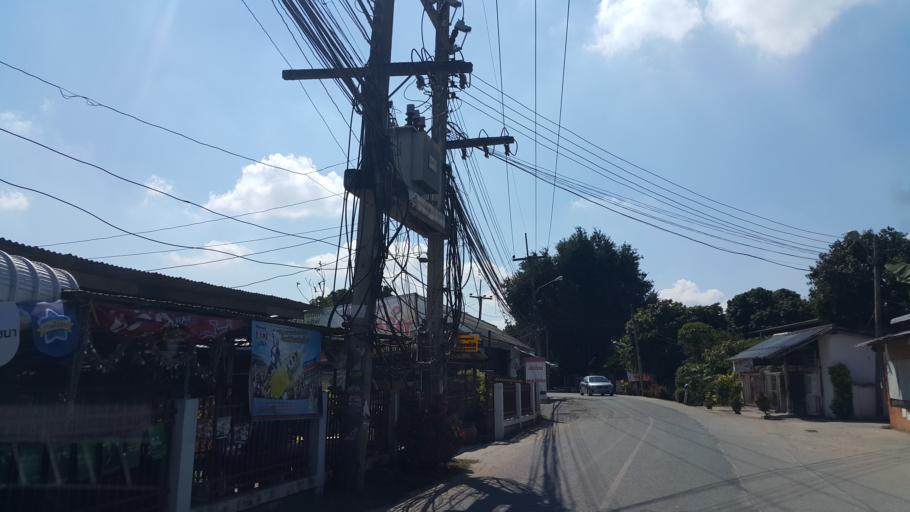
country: TH
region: Chiang Mai
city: San Sai
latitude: 18.8378
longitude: 99.0178
